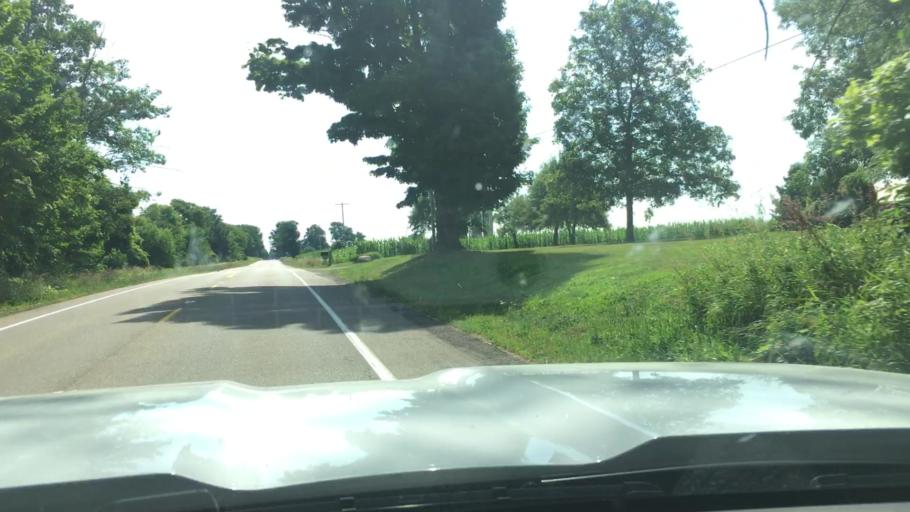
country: US
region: Michigan
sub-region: Kent County
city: Lowell
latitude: 42.8856
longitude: -85.3606
